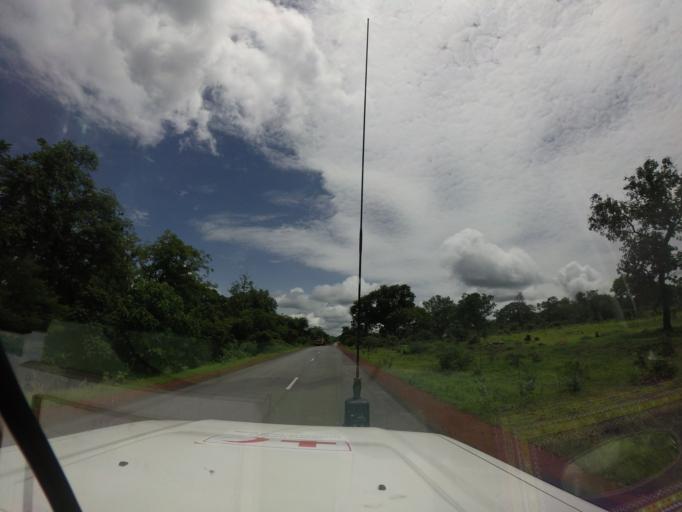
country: SL
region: Northern Province
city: Gberia Fotombu
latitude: 10.0581
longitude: -11.0102
